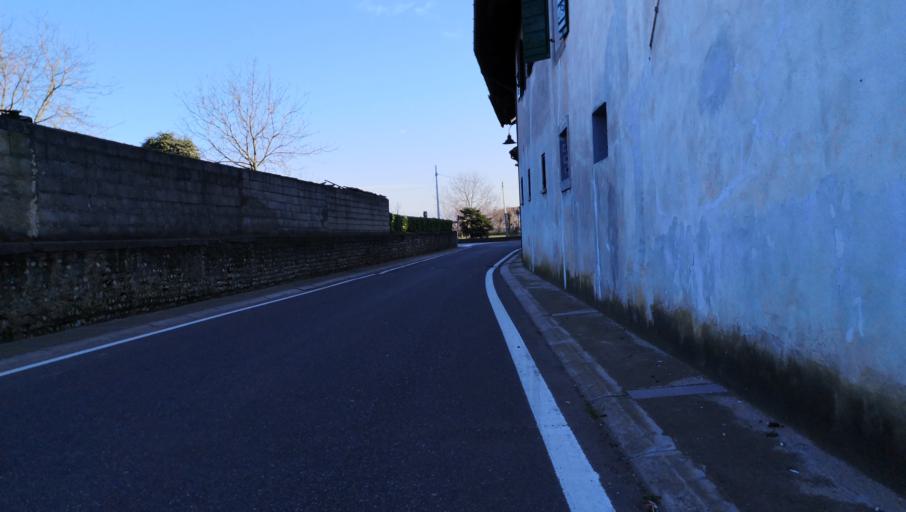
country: IT
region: Friuli Venezia Giulia
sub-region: Provincia di Udine
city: Lauzacco
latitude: 45.9655
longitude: 13.2979
